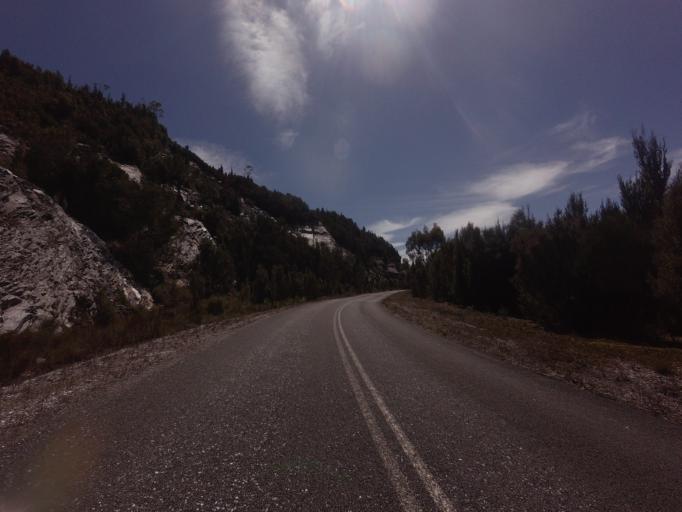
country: AU
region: Tasmania
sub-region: West Coast
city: Queenstown
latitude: -42.7542
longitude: 145.9994
